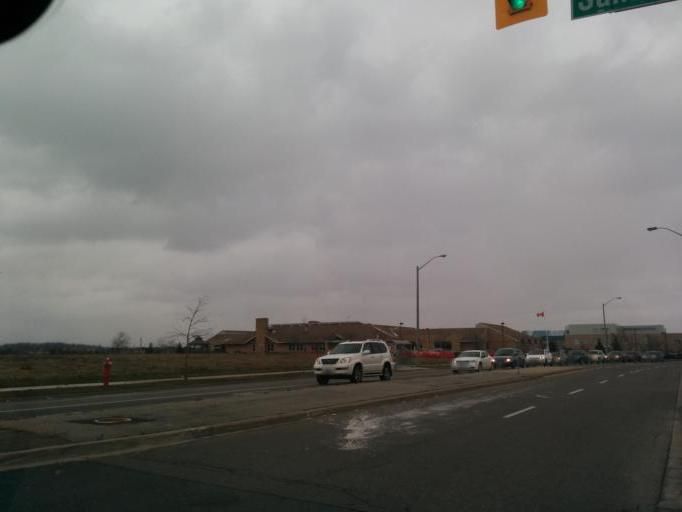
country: CA
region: Ontario
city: Brampton
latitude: 43.7414
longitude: -79.7738
